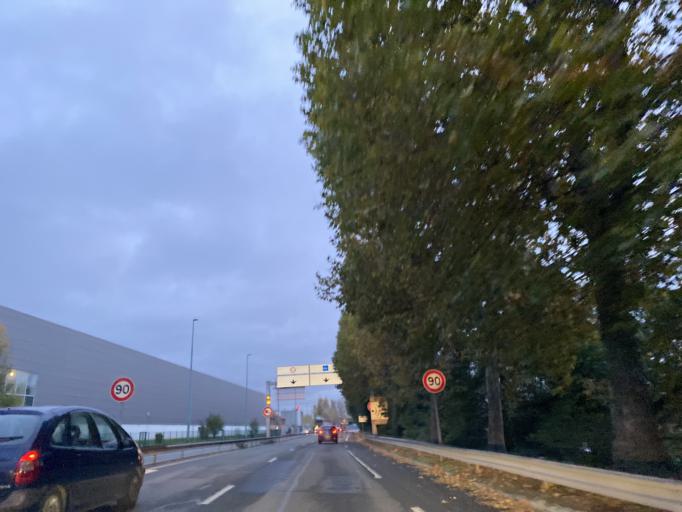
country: FR
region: Ile-de-France
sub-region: Departement des Hauts-de-Seine
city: Colombes
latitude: 48.9314
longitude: 2.2366
